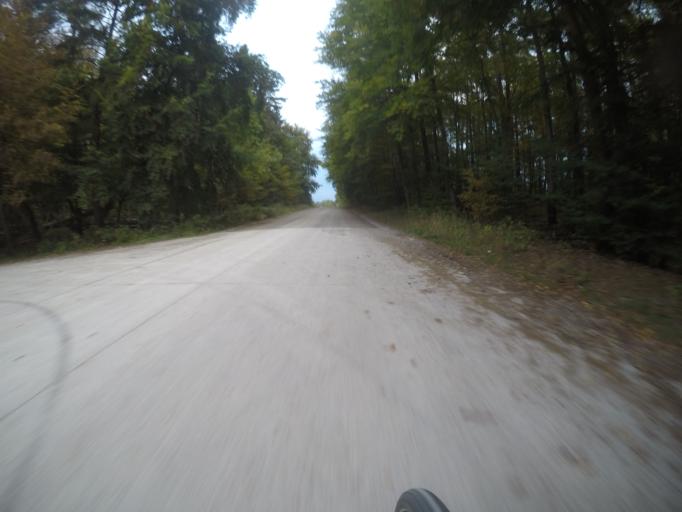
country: DE
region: Baden-Wuerttemberg
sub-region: Regierungsbezirk Stuttgart
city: Schonaich
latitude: 48.6880
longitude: 9.0633
